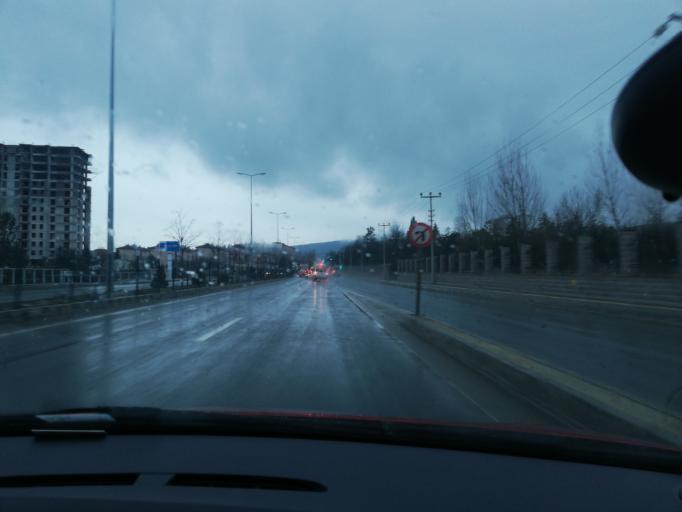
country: TR
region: Kastamonu
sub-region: Cide
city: Kastamonu
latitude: 41.4122
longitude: 33.7926
